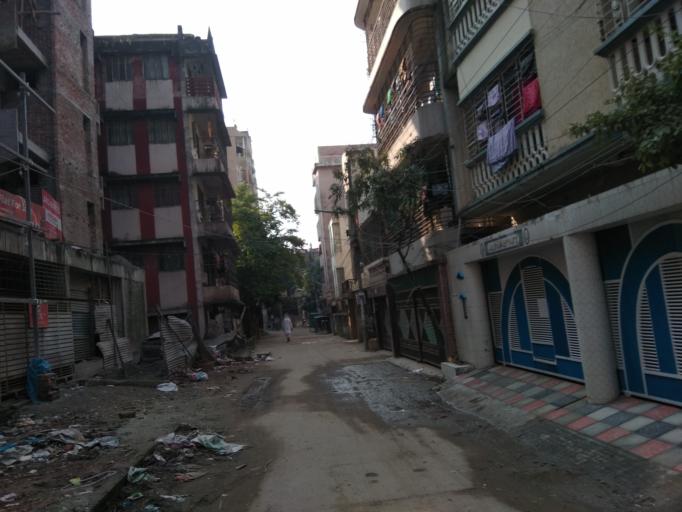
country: BD
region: Dhaka
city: Tungi
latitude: 23.8260
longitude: 90.3606
